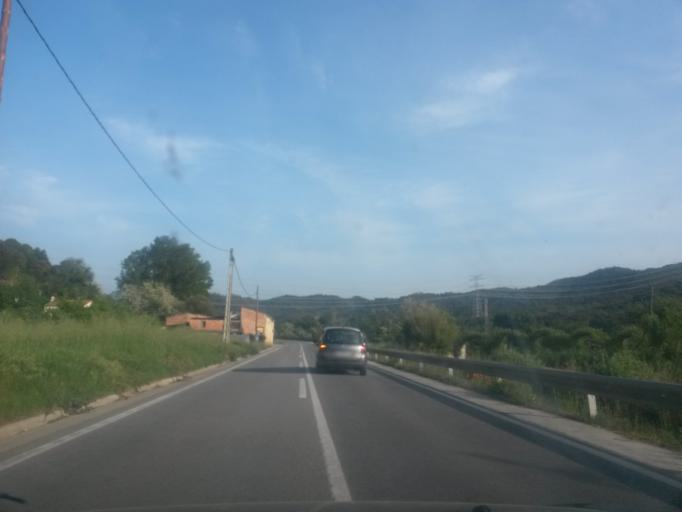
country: ES
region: Catalonia
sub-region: Provincia de Girona
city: Sant Gregori
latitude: 41.9771
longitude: 2.7094
